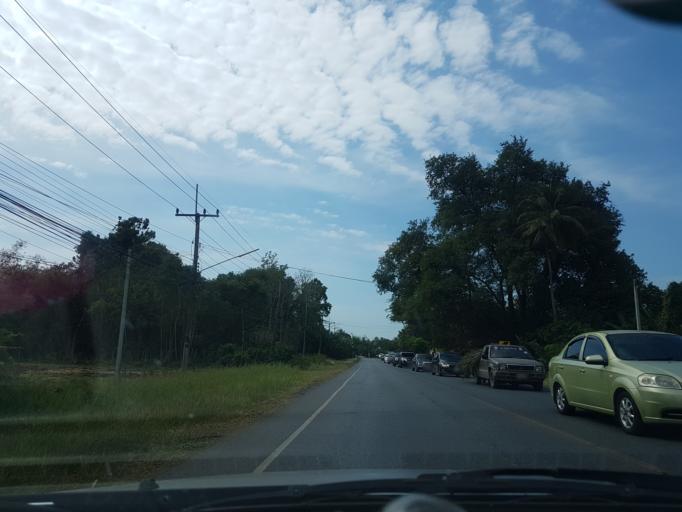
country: TH
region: Lop Buri
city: Lop Buri
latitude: 14.8021
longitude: 100.7452
